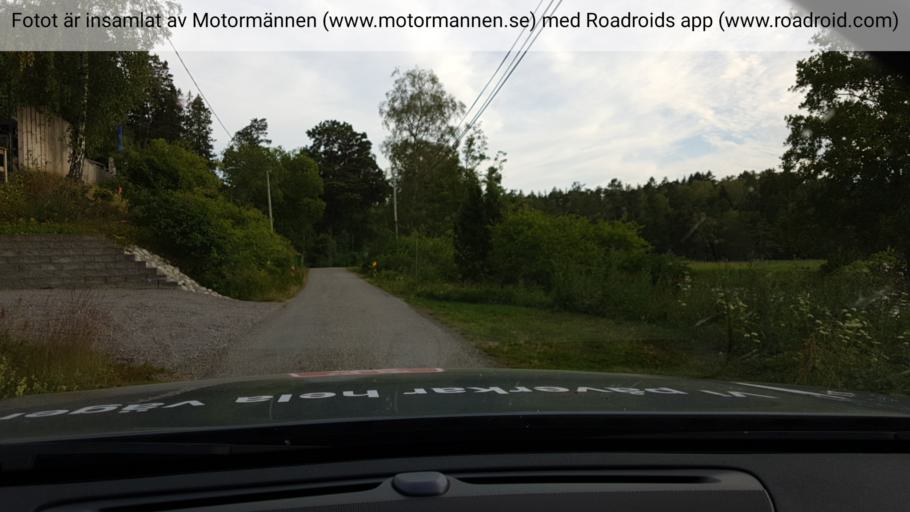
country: SE
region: Stockholm
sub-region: Haninge Kommun
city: Jordbro
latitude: 59.0181
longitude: 18.0946
